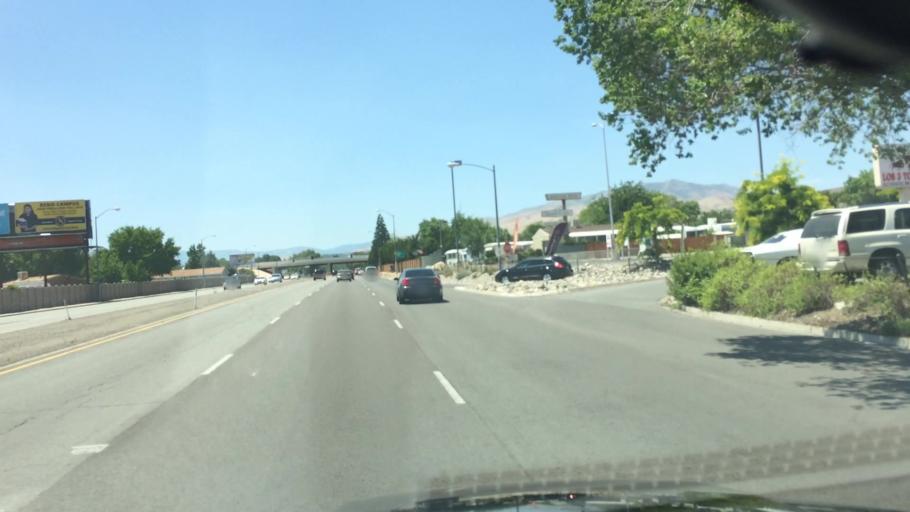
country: US
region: Nevada
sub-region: Washoe County
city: Sparks
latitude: 39.5456
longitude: -119.7838
